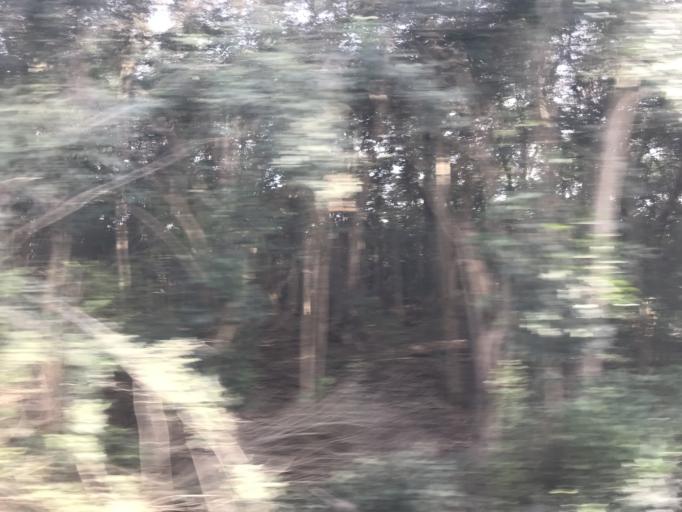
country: AR
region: Cordoba
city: Laguna Larga
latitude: -31.8020
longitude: -63.7810
